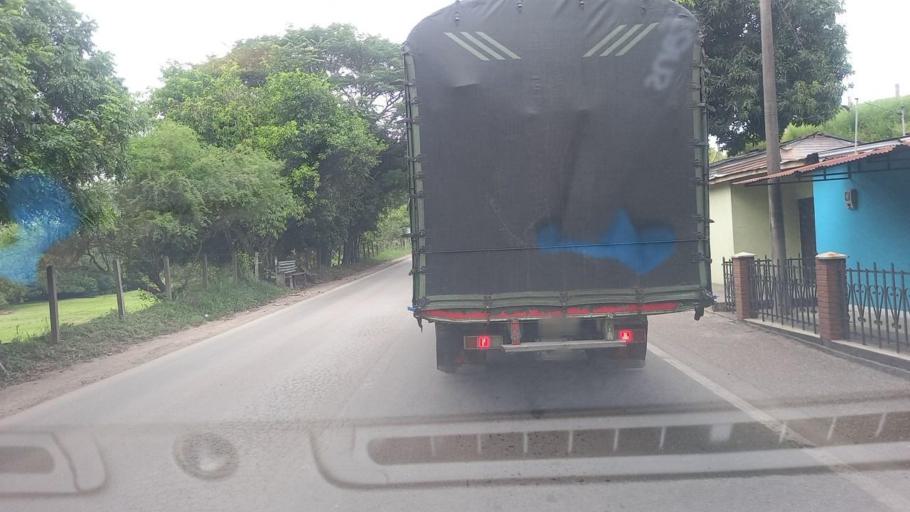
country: CO
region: Boyaca
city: Puerto Boyaca
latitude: 5.9307
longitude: -74.5686
